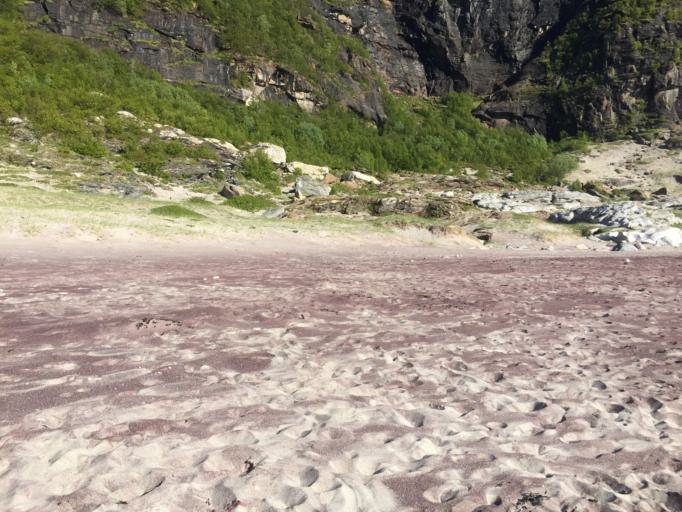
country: NO
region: Nordland
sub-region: Bodo
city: Loding
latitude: 67.4232
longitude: 14.6355
